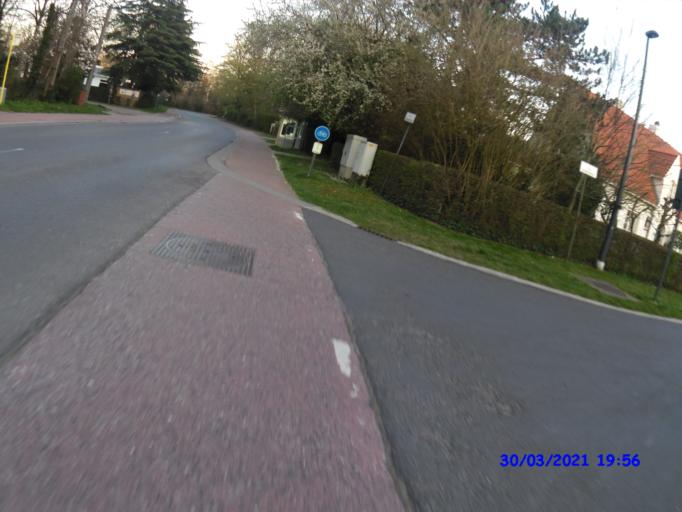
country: BE
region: Flanders
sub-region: Provincie Oost-Vlaanderen
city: Sint-Martens-Latem
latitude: 51.0287
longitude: 3.6690
